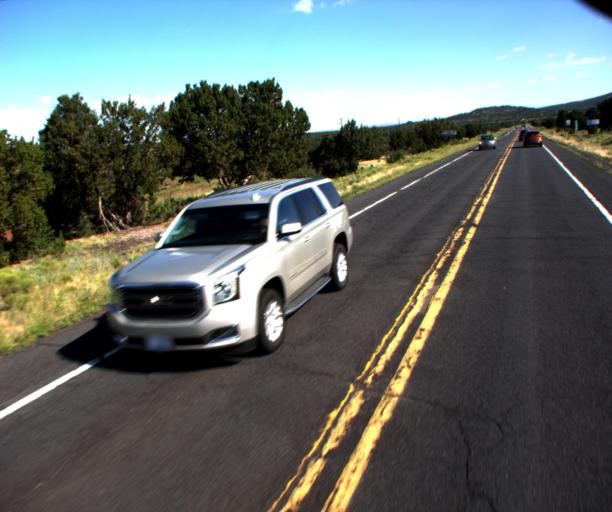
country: US
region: Arizona
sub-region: Coconino County
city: Williams
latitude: 35.3483
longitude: -112.1667
